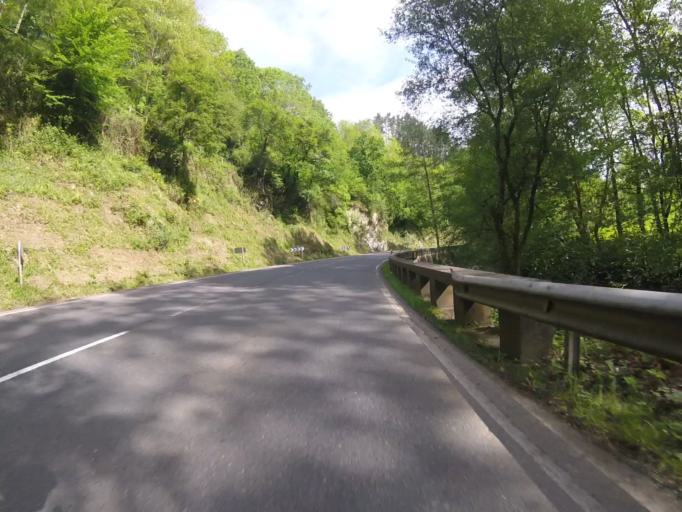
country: ES
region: Basque Country
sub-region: Provincia de Guipuzcoa
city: Azkoitia
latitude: 43.1593
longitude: -2.3348
